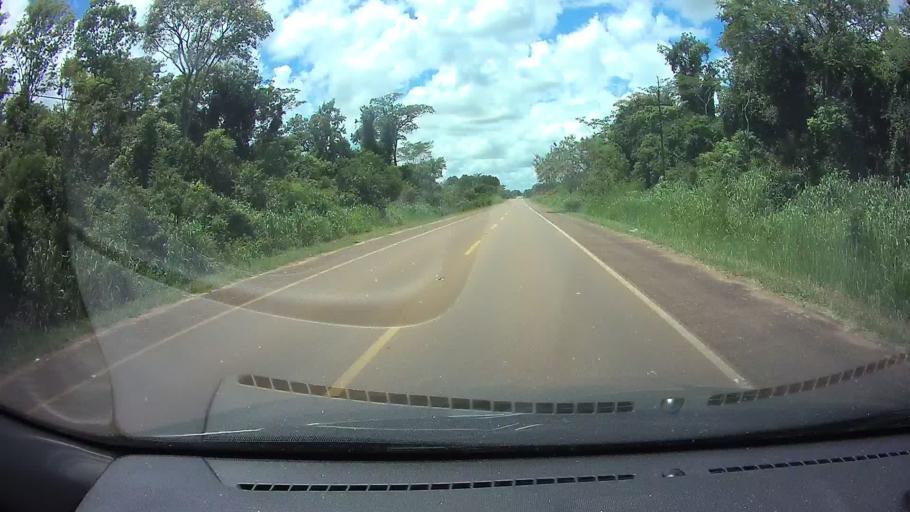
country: PY
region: Paraguari
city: La Colmena
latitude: -25.8912
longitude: -56.8181
